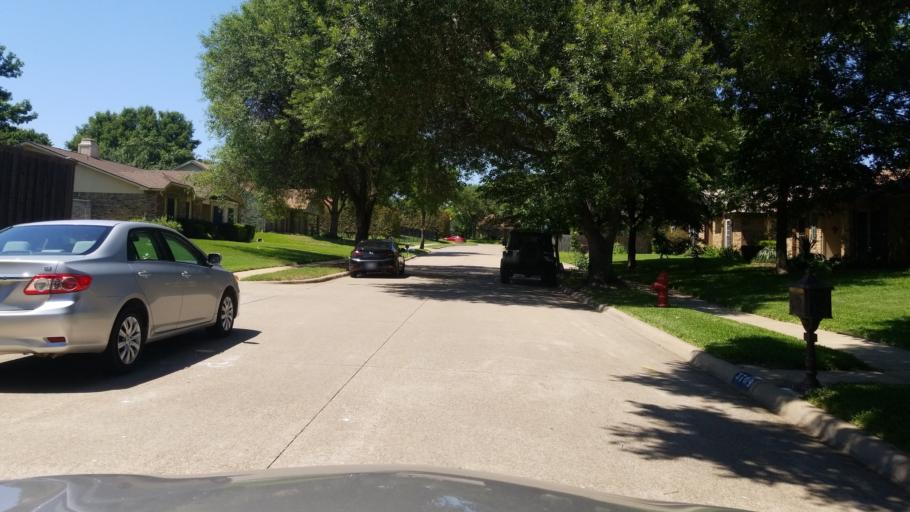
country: US
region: Texas
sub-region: Dallas County
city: Grand Prairie
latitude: 32.6837
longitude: -97.0039
